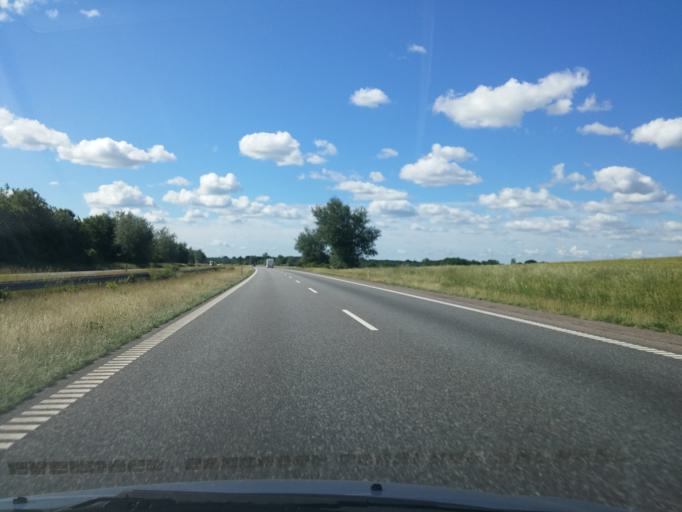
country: DK
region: South Denmark
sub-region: Kolding Kommune
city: Christiansfeld
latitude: 55.4155
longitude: 9.4560
